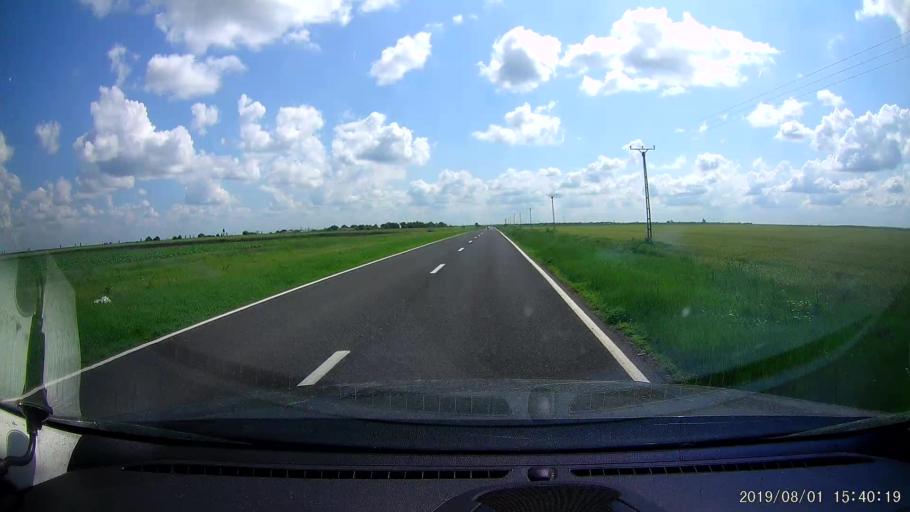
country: RO
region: Braila
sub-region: Comuna Baraganul
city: Baraganul
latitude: 44.8398
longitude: 27.5444
